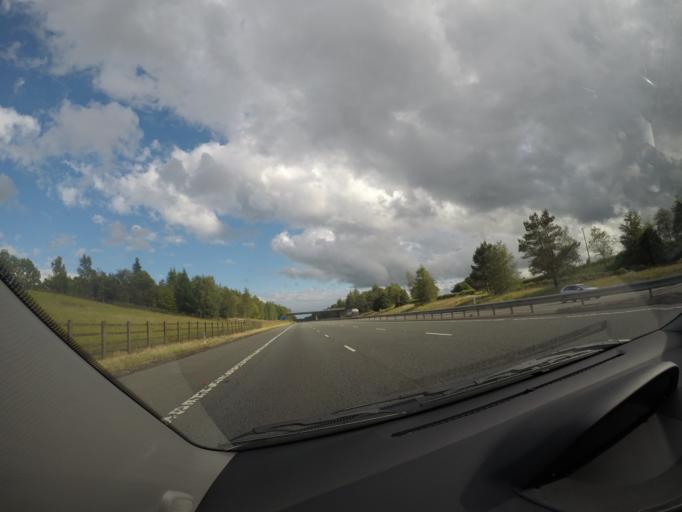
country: GB
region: Scotland
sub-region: Dumfries and Galloway
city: Lockerbie
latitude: 55.1259
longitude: -3.3650
